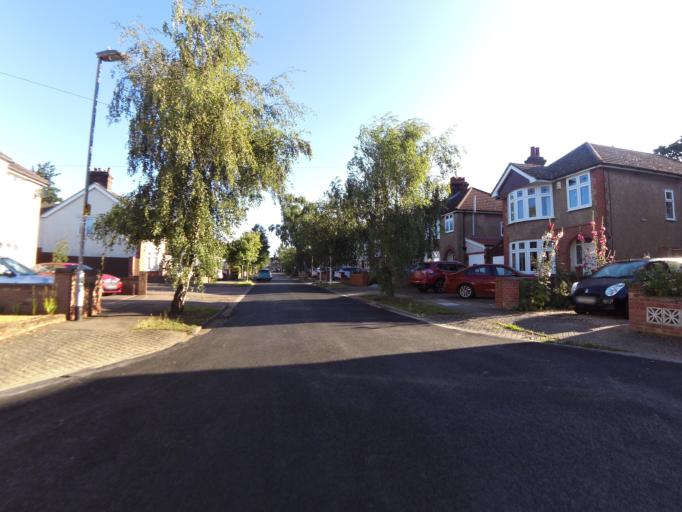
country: GB
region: England
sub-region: Suffolk
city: Ipswich
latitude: 52.0657
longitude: 1.1879
